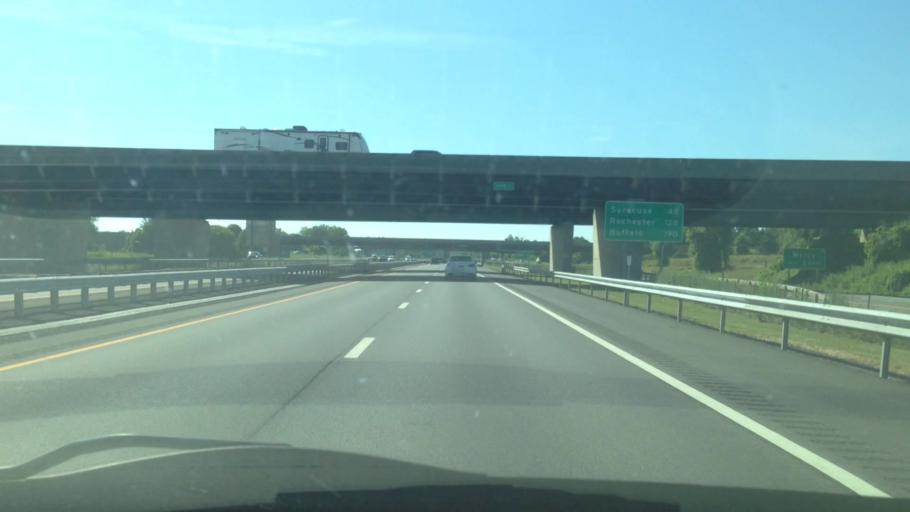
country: US
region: New York
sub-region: Oneida County
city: Utica
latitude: 43.1217
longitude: -75.2297
